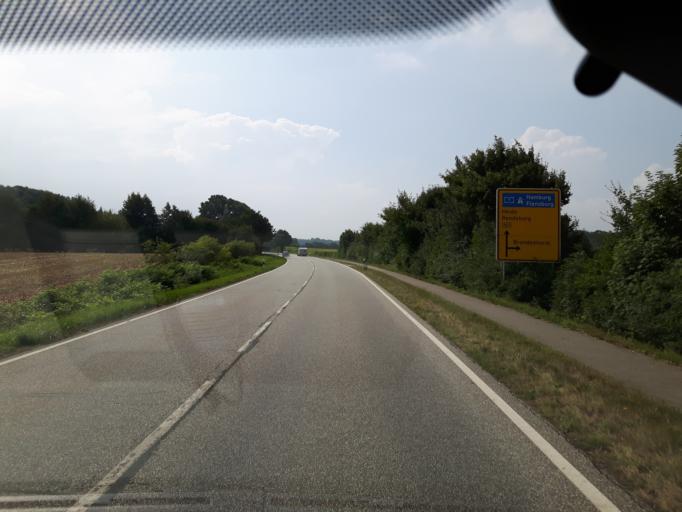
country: DE
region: Schleswig-Holstein
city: Goosefeld
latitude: 54.4201
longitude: 9.8018
